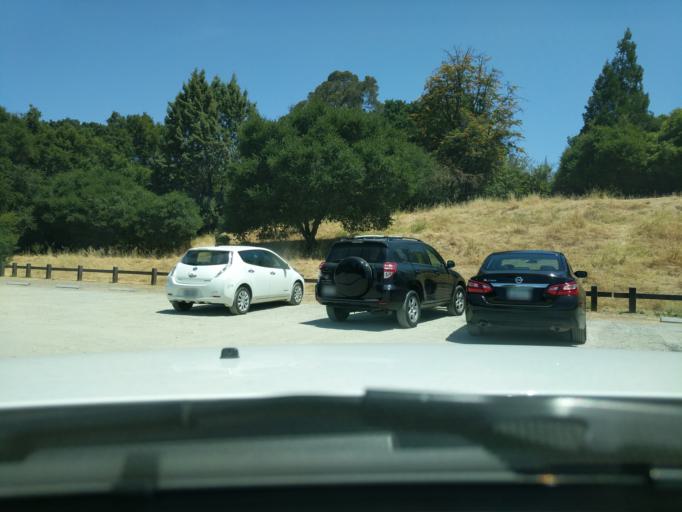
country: US
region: California
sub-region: Alameda County
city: Union City
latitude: 37.6073
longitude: -122.0176
